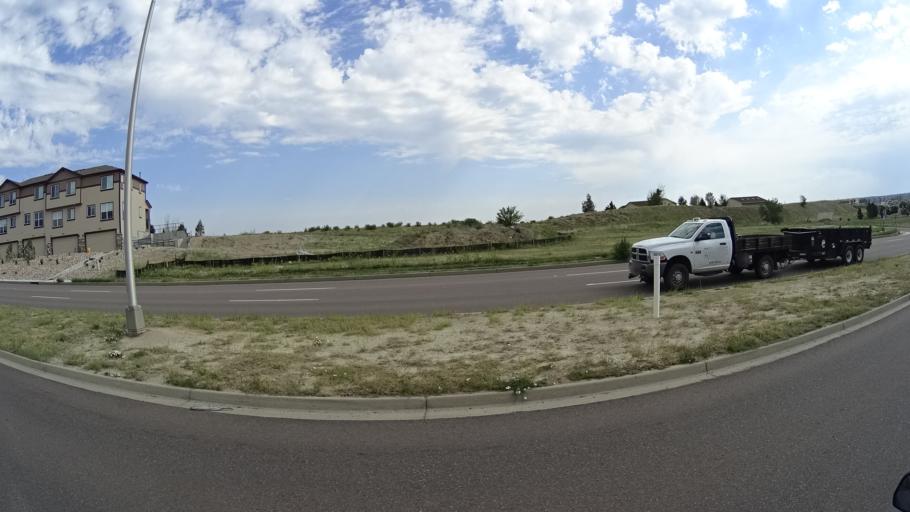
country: US
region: Colorado
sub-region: El Paso County
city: Cimarron Hills
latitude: 38.9123
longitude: -104.7249
